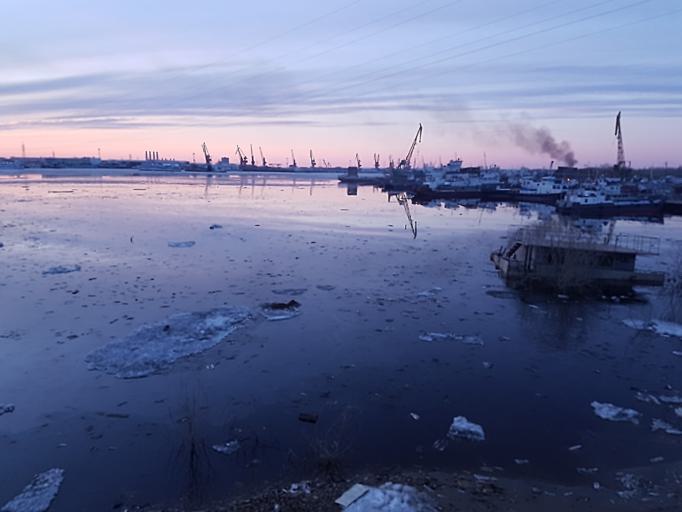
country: RU
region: Sakha
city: Yakutsk
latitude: 62.0377
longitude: 129.7729
